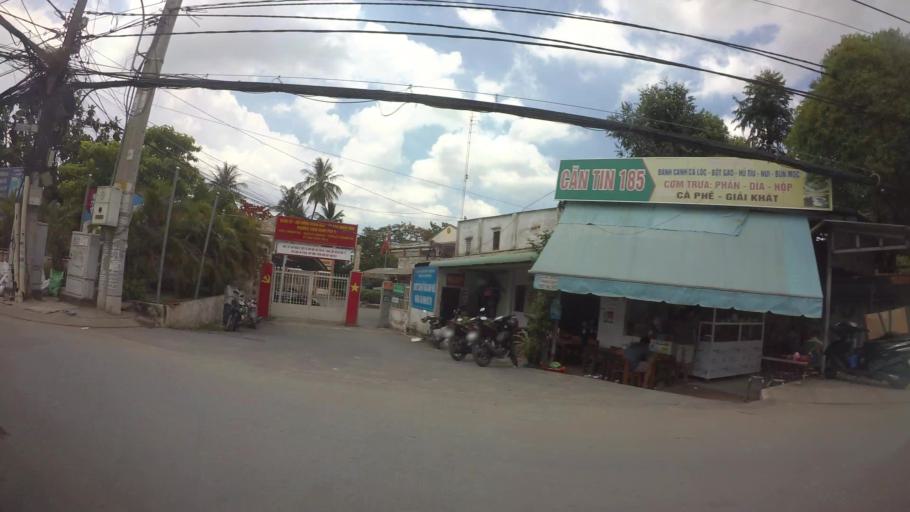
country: VN
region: Ho Chi Minh City
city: Quan Chin
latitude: 10.8332
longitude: 106.7837
